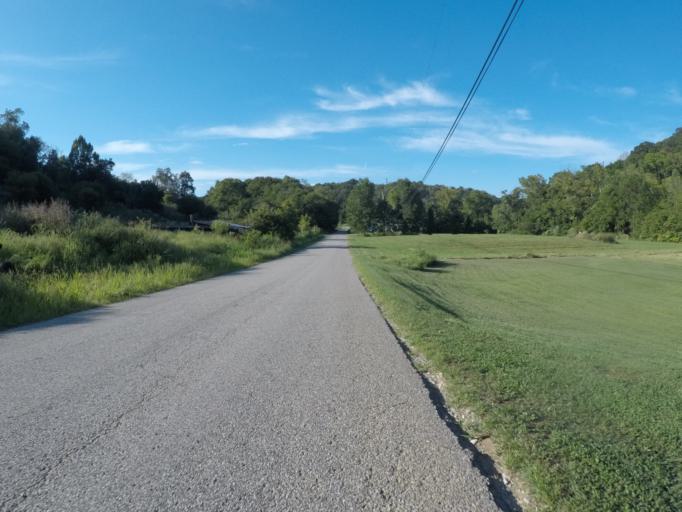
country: US
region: West Virginia
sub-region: Cabell County
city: Huntington
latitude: 38.4993
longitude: -82.4880
